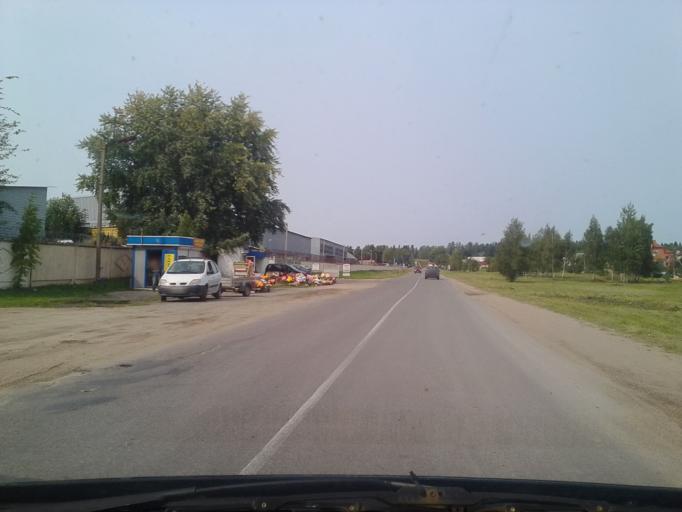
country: BY
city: Michanovichi
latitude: 53.7585
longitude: 27.6787
